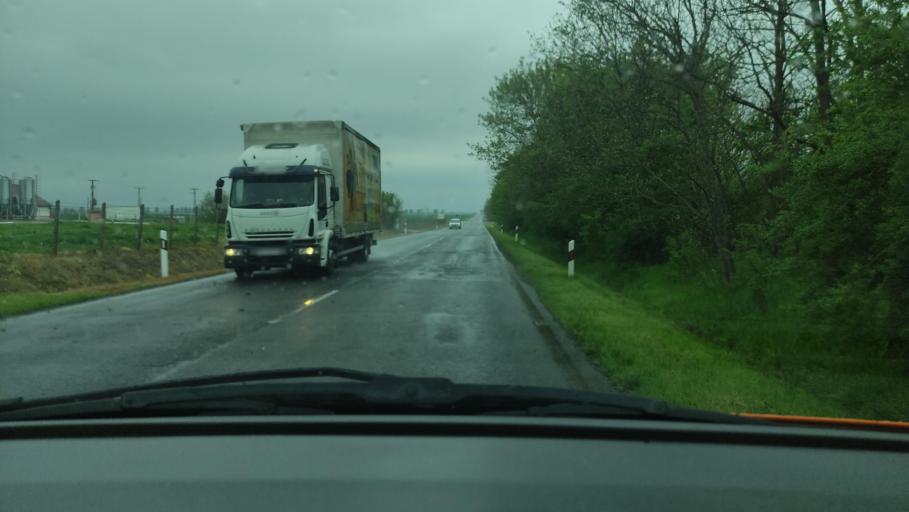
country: HU
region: Baranya
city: Mohacs
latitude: 45.9278
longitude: 18.6596
